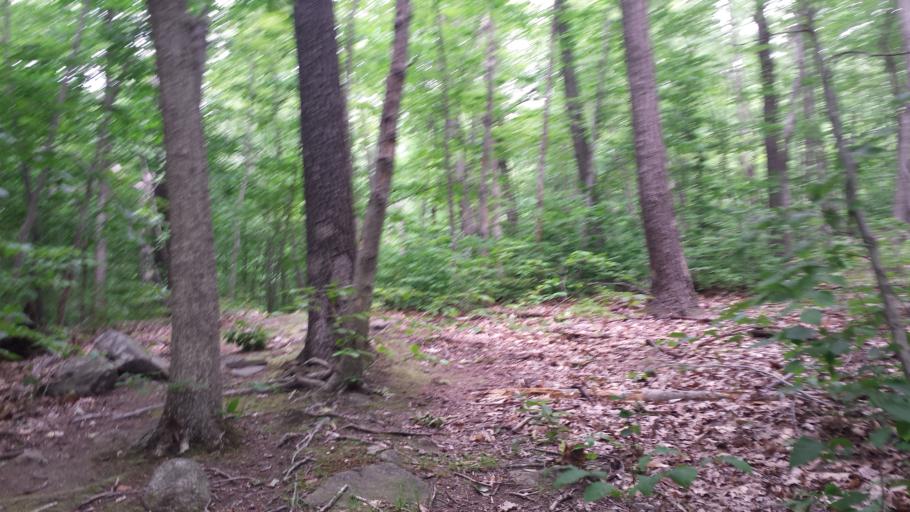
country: US
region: New York
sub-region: Putnam County
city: Peach Lake
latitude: 41.3122
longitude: -73.5671
